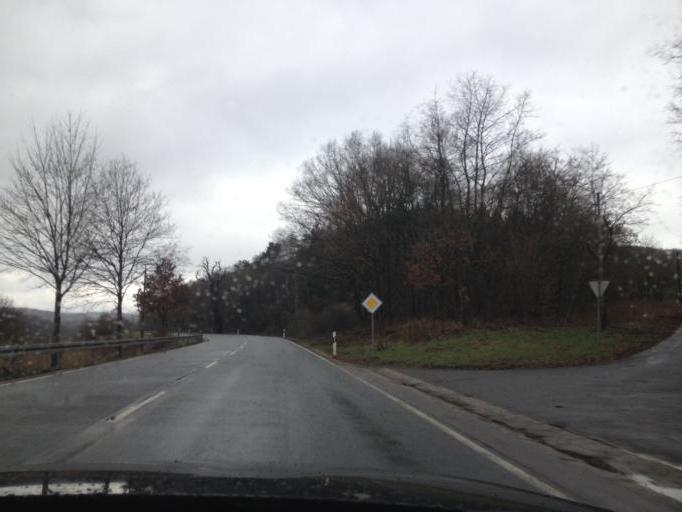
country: DE
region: Saarland
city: Nohfelden
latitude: 49.5753
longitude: 7.1657
